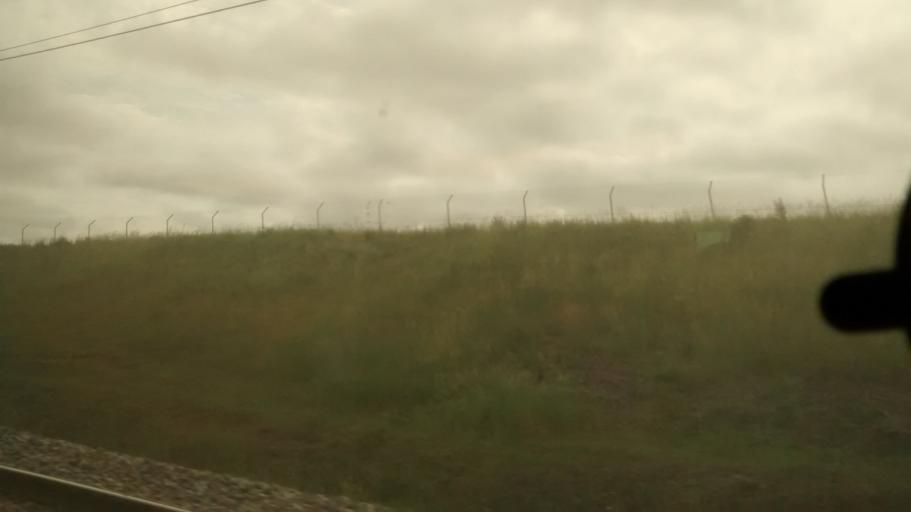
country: FR
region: Ile-de-France
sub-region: Departement des Yvelines
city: Ablis
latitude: 48.4926
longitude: 1.8907
